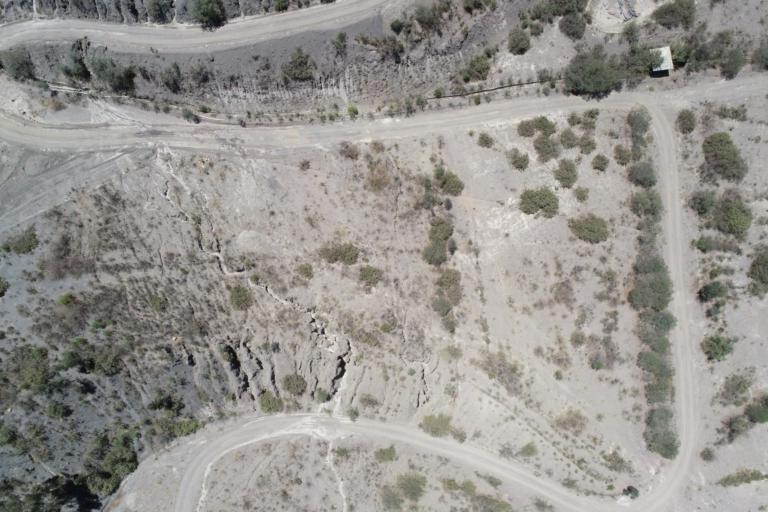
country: BO
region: La Paz
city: La Paz
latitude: -16.6145
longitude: -68.0610
